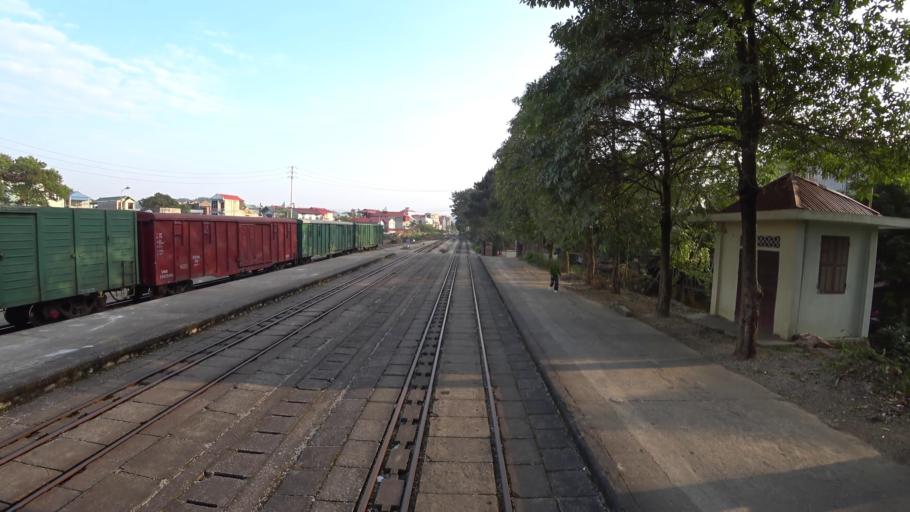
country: VN
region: Lang Son
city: Thi Tran Cao Loc
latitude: 21.8639
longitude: 106.7649
